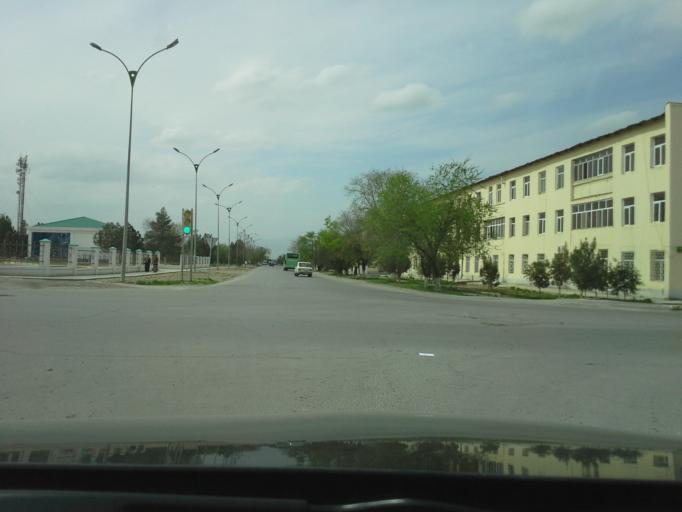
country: TM
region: Ahal
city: Abadan
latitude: 38.0581
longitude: 58.1503
